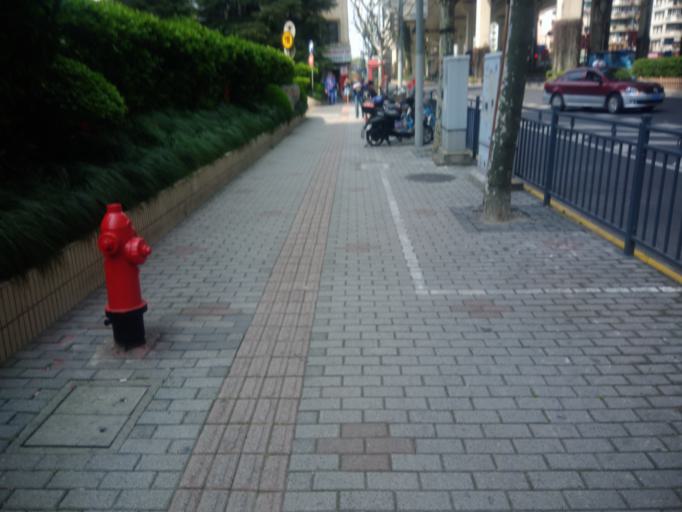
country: CN
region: Shanghai Shi
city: Luwan
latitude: 31.2001
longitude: 121.4722
